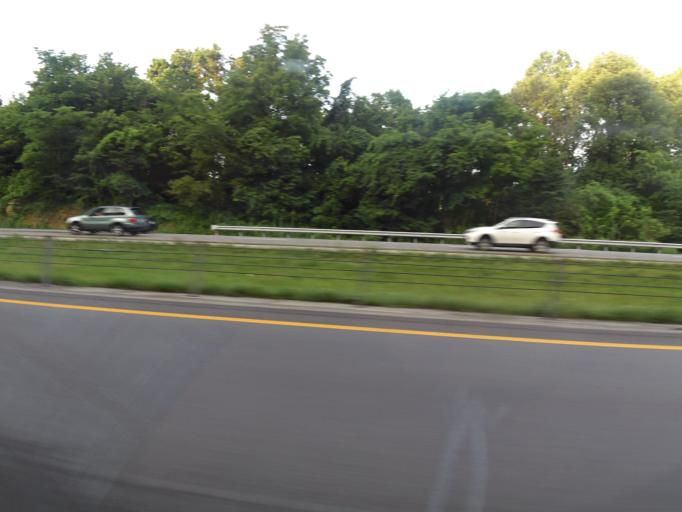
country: US
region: Kentucky
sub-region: Rockcastle County
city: Mount Vernon
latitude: 37.3897
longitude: -84.3363
